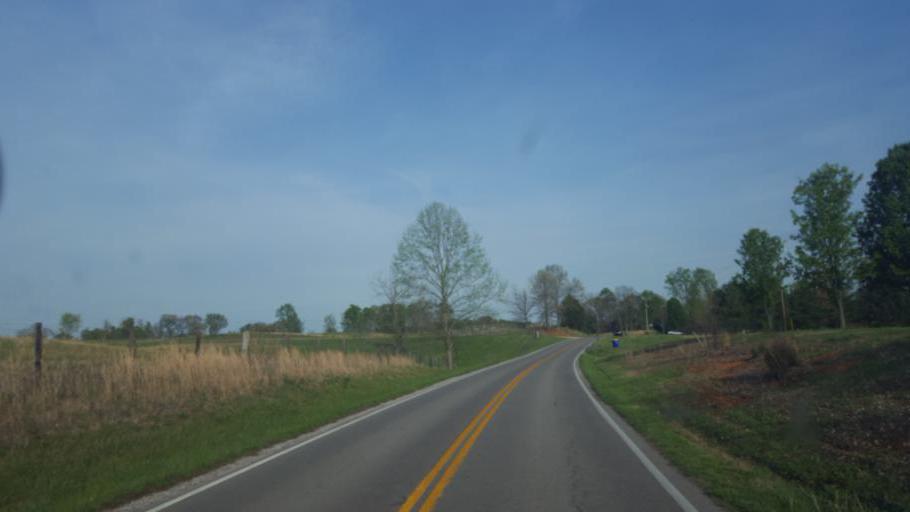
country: US
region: Kentucky
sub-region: Warren County
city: Plano
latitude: 36.9290
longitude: -86.2866
